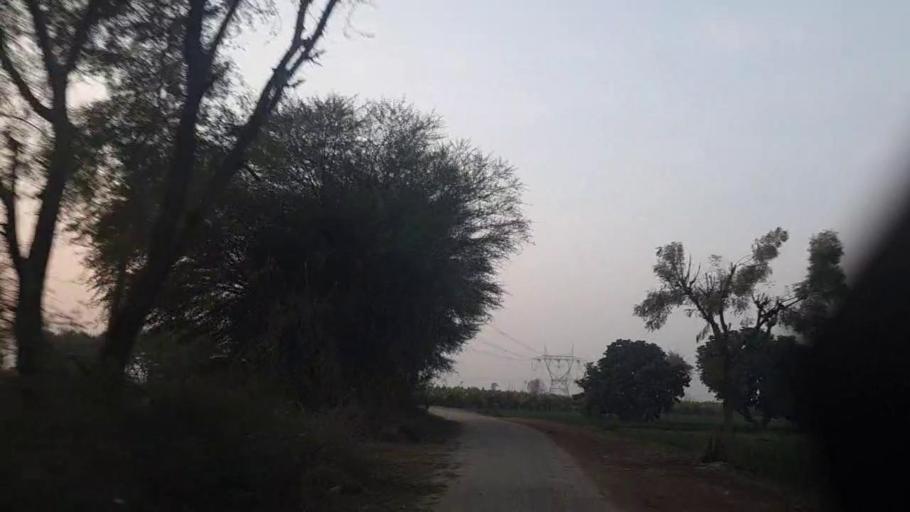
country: PK
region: Sindh
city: Sakrand
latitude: 26.1003
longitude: 68.3232
